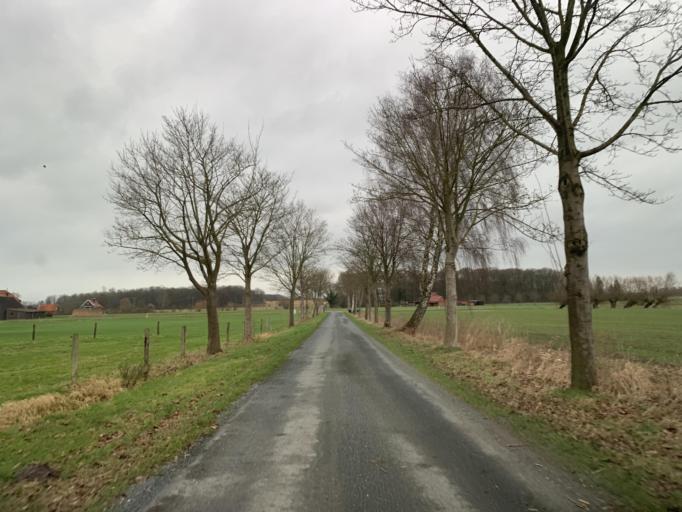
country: DE
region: North Rhine-Westphalia
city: Ludinghausen
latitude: 51.8104
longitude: 7.4684
